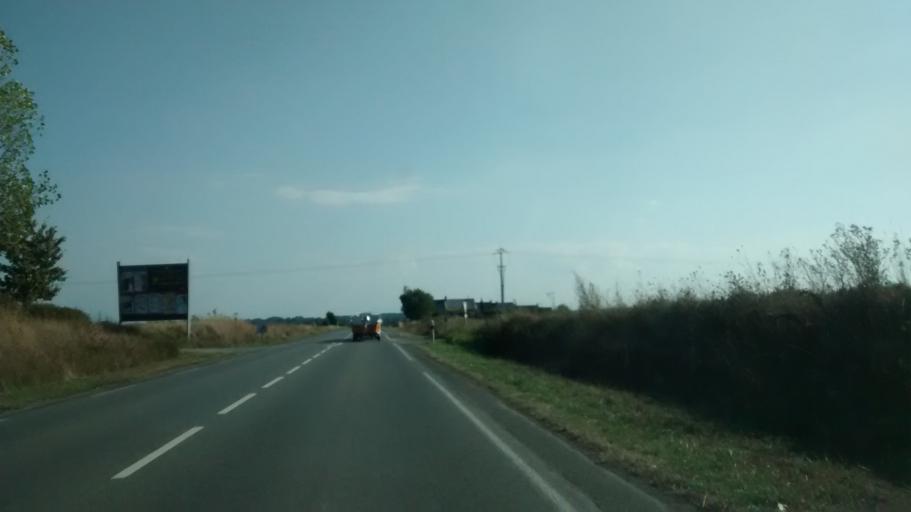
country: FR
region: Brittany
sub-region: Departement d'Ille-et-Vilaine
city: Saint-Meloir-des-Ondes
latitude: 48.6261
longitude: -1.9045
